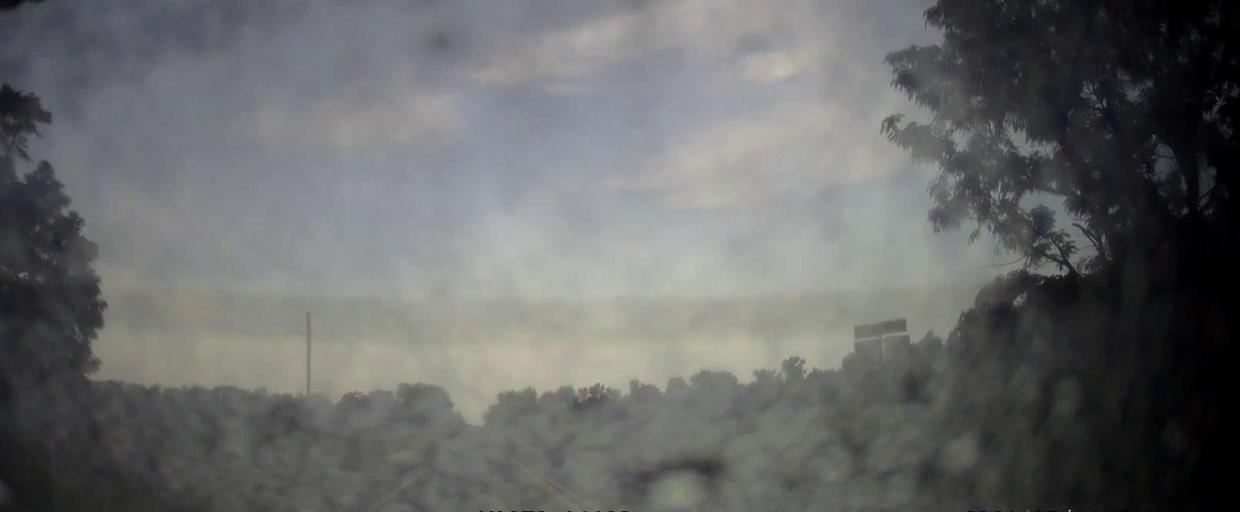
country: US
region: Georgia
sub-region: Dodge County
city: Chester
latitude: 32.5467
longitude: -83.1181
